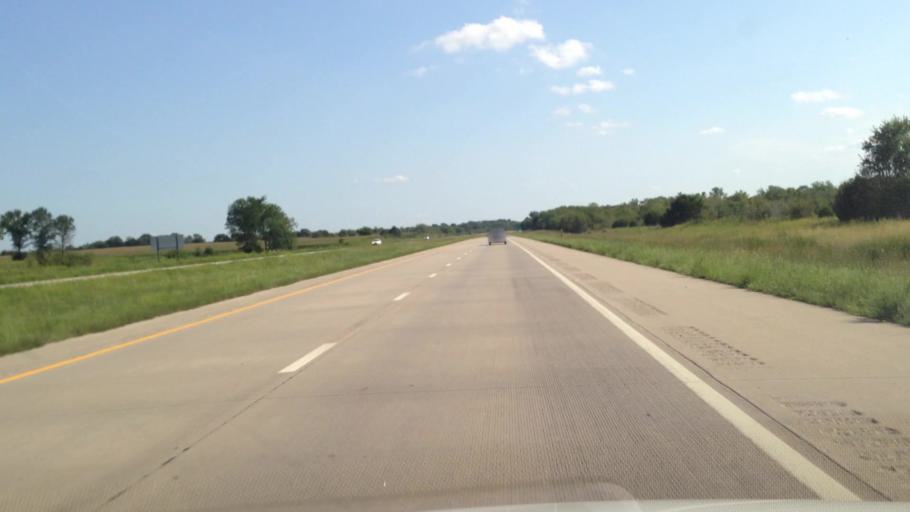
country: US
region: Kansas
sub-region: Bourbon County
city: Fort Scott
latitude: 37.9171
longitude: -94.7044
